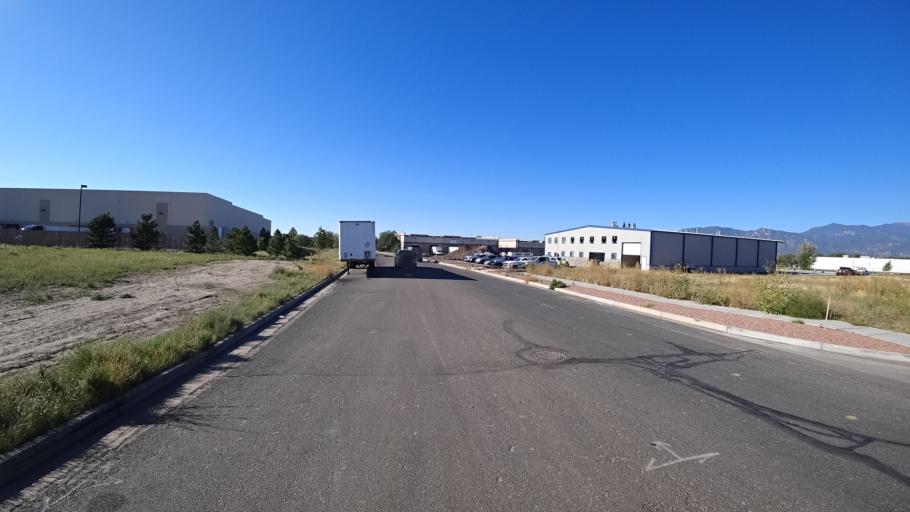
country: US
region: Colorado
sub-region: El Paso County
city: Cimarron Hills
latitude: 38.8150
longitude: -104.7282
